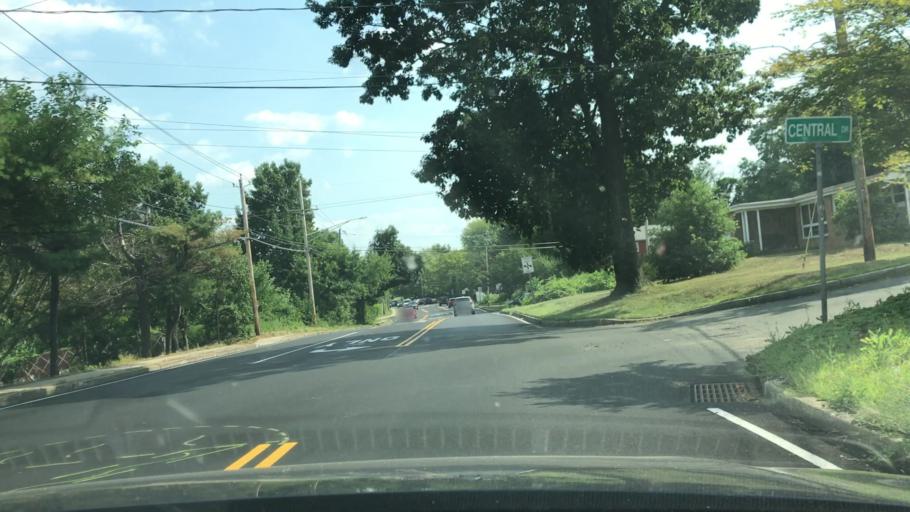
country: US
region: New York
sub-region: Rockland County
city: Bardonia
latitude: 41.1146
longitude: -74.0104
